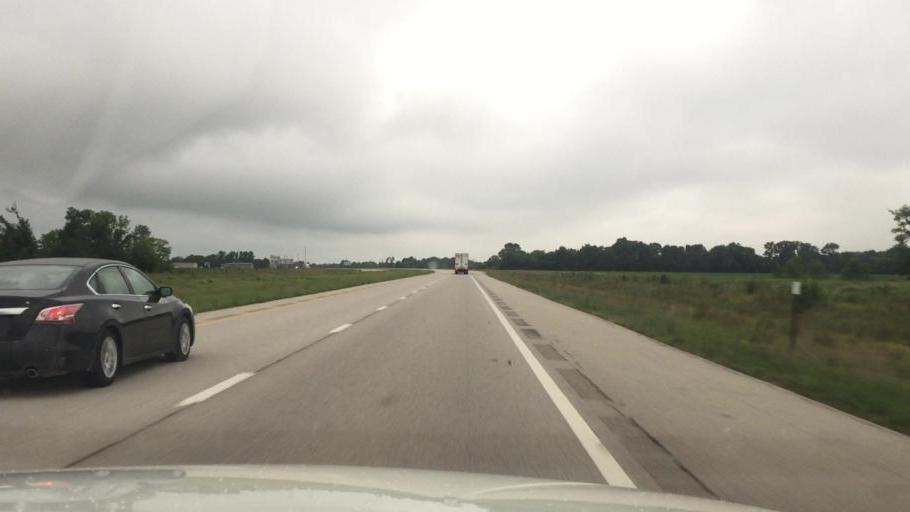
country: US
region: Kansas
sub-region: Montgomery County
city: Coffeyville
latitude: 37.1054
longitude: -95.5880
